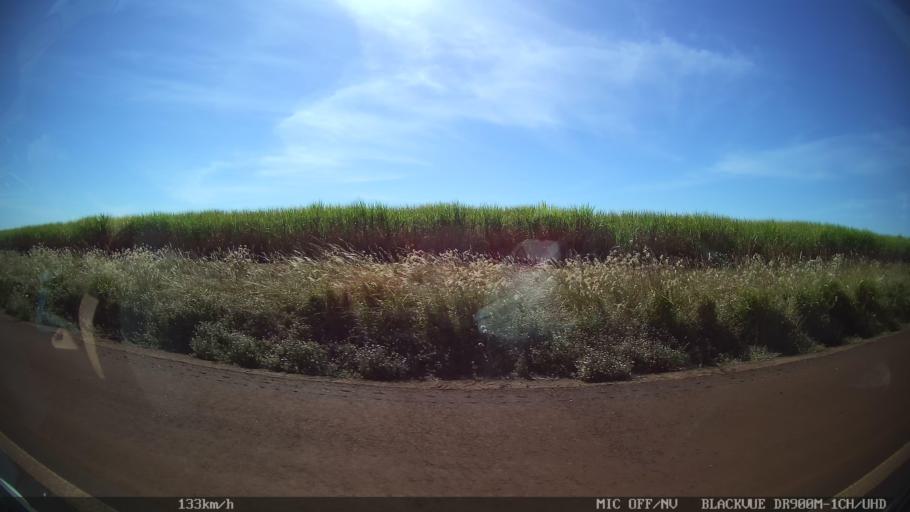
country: BR
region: Sao Paulo
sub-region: Guaira
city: Guaira
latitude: -20.4439
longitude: -48.3527
